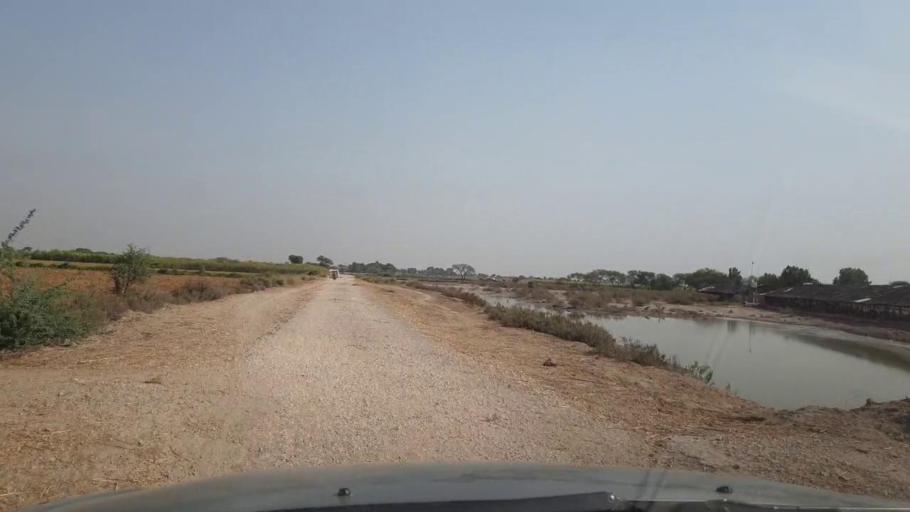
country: PK
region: Sindh
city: Bulri
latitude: 24.9131
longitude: 68.3648
